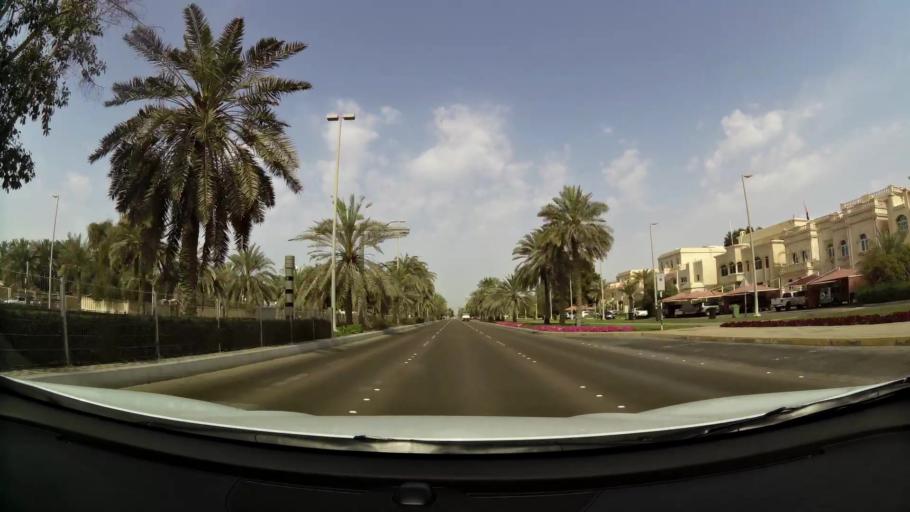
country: AE
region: Abu Dhabi
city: Abu Dhabi
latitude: 24.4399
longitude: 54.3659
